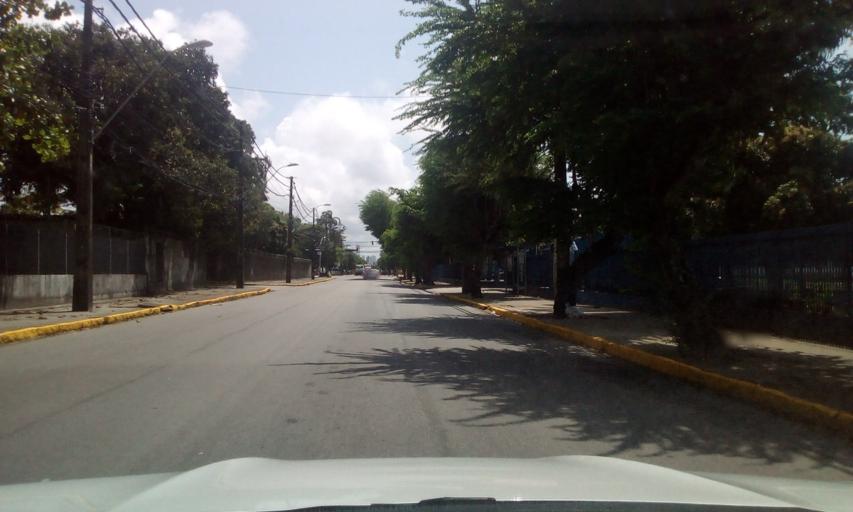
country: BR
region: Pernambuco
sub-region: Recife
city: Recife
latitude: -8.0619
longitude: -34.9262
